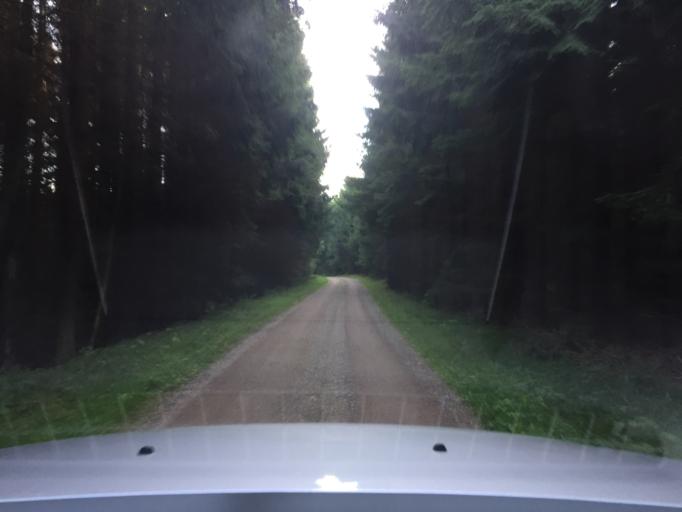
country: SE
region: Skane
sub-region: Hassleholms Kommun
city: Sosdala
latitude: 56.0142
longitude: 13.7077
